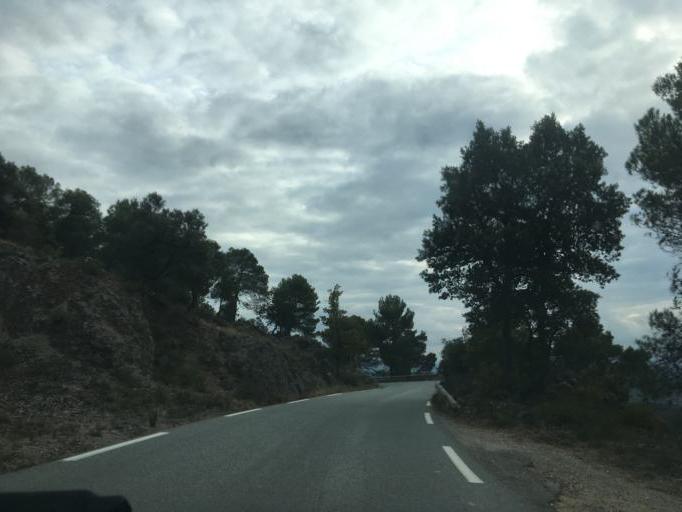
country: FR
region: Provence-Alpes-Cote d'Azur
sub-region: Departement du Var
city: Villecroze
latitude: 43.5824
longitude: 6.3102
